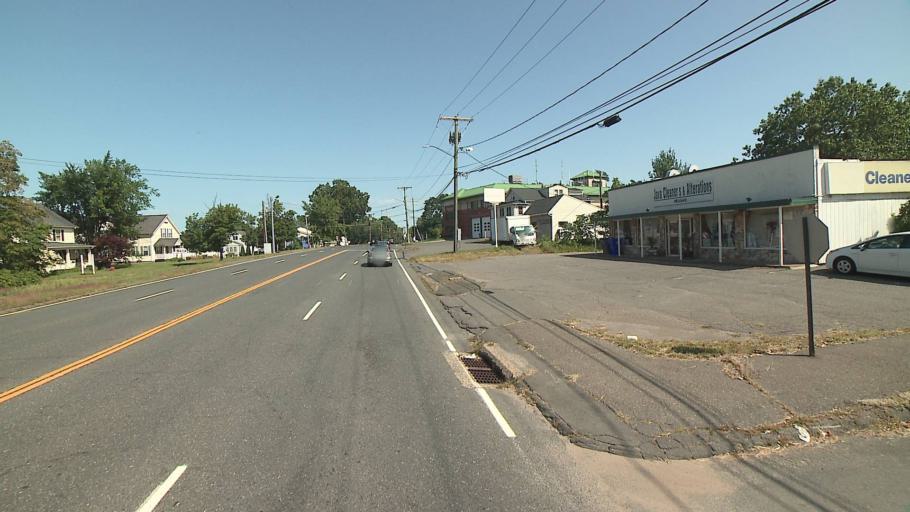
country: US
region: Connecticut
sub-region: Hartford County
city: Thompsonville
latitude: 42.0120
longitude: -72.5935
